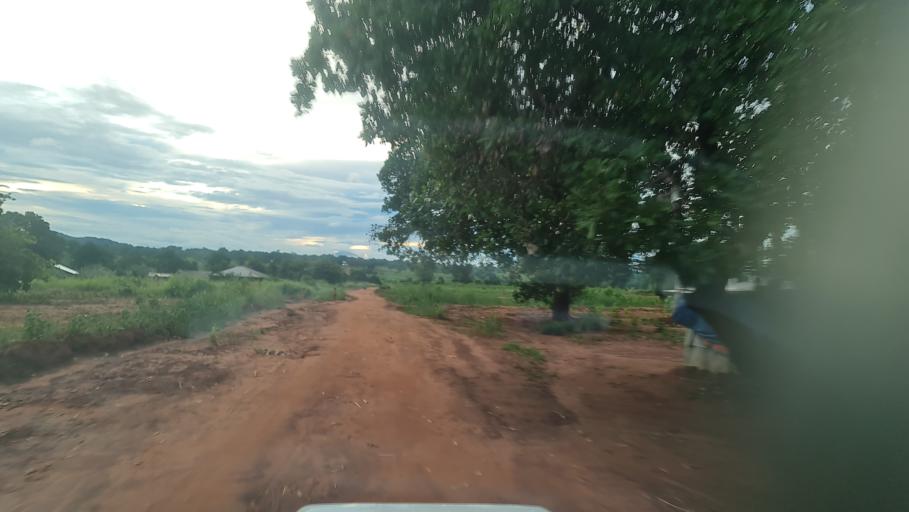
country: MZ
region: Nampula
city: Nacala
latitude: -14.7437
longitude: 39.9528
